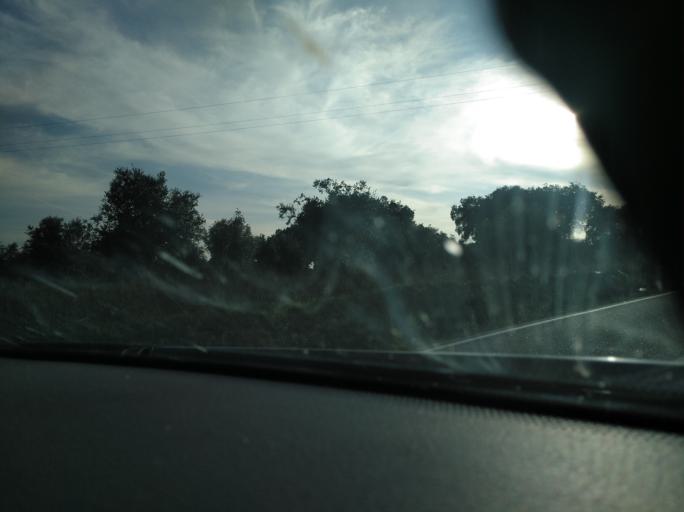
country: PT
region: Portalegre
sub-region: Fronteira
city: Fronteira
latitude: 38.9614
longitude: -7.5806
